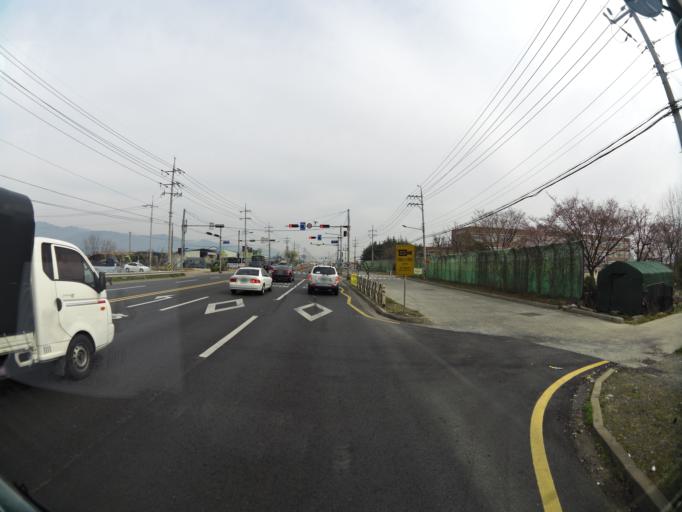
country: KR
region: Gyeongsangbuk-do
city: Gyeongsan-si
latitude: 35.8613
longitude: 128.7718
